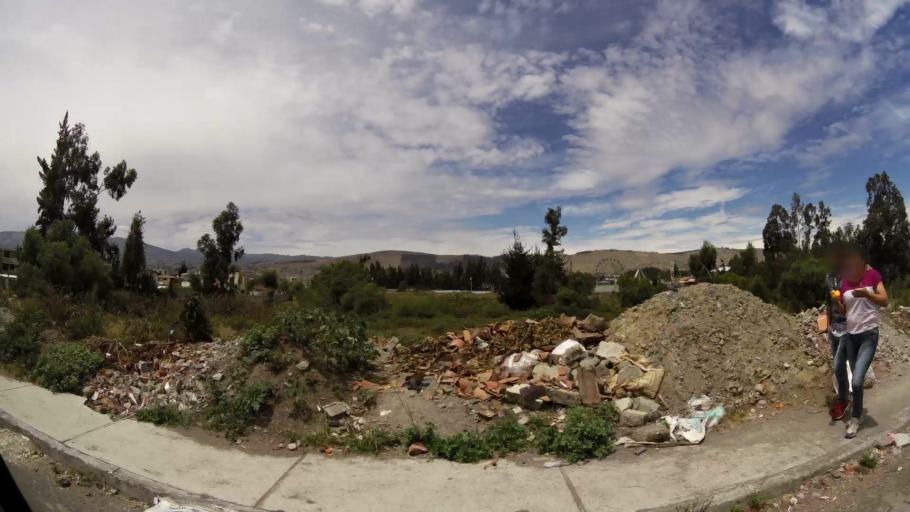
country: EC
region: Cotopaxi
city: San Miguel de Salcedo
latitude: -1.0405
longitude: -78.5868
